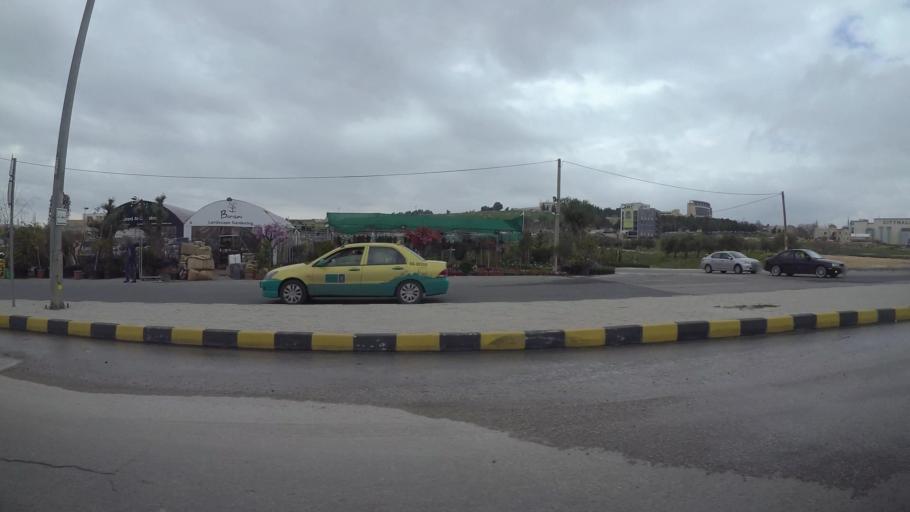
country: JO
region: Amman
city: Wadi as Sir
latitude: 31.9762
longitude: 35.8403
